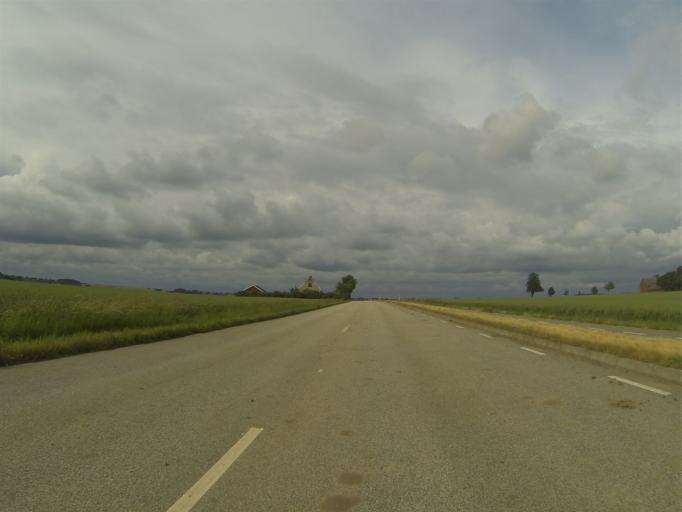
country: SE
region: Skane
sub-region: Eslovs Kommun
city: Eslov
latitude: 55.7575
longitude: 13.3040
